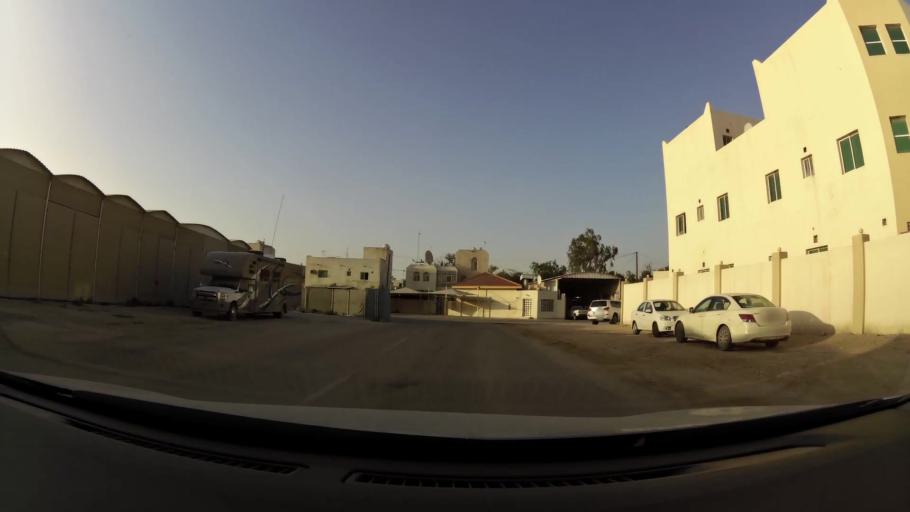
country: QA
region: Baladiyat ar Rayyan
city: Ar Rayyan
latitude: 25.3248
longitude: 51.4595
